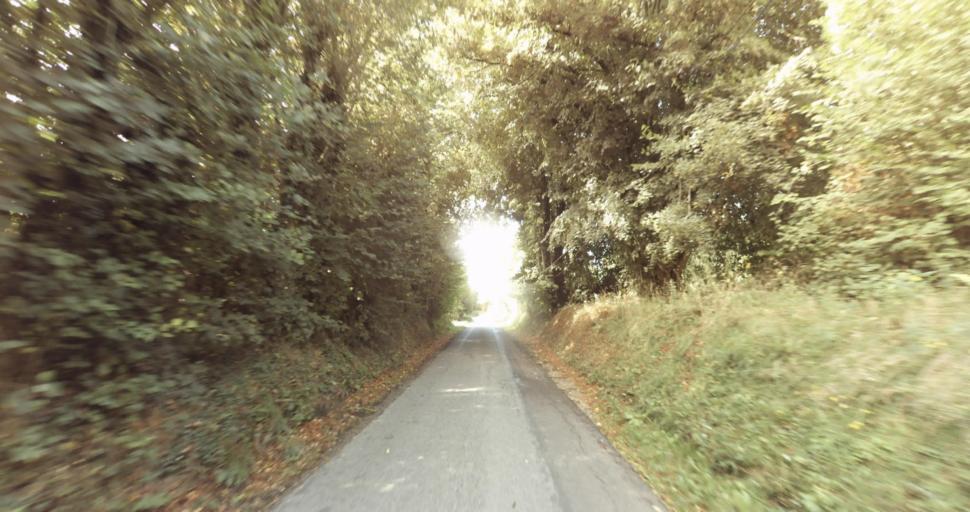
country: FR
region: Lower Normandy
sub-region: Departement de l'Orne
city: Gace
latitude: 48.7879
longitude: 0.3098
